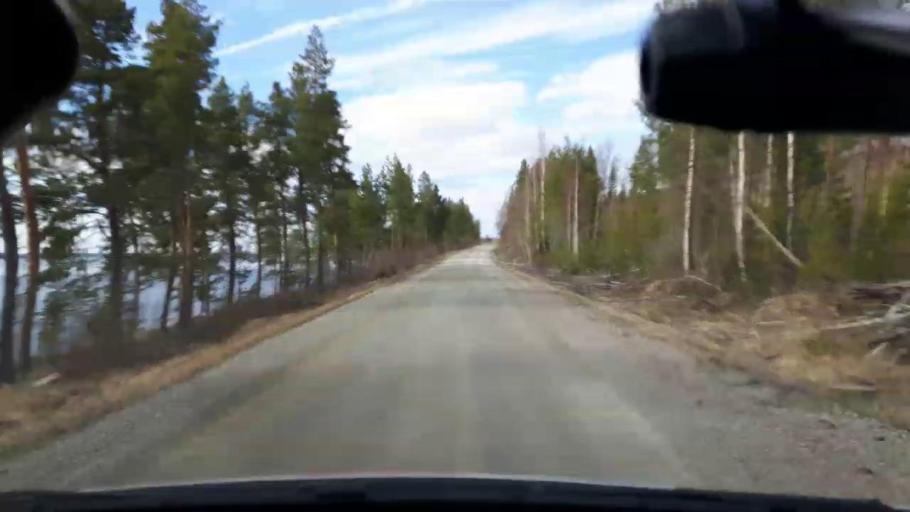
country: SE
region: Jaemtland
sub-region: Bergs Kommun
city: Hoverberg
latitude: 62.7286
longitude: 14.6659
